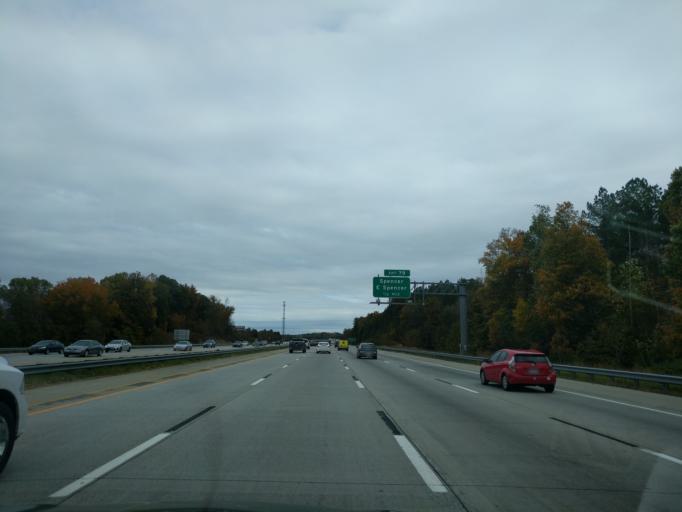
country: US
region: North Carolina
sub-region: Rowan County
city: East Spencer
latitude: 35.6717
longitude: -80.4293
